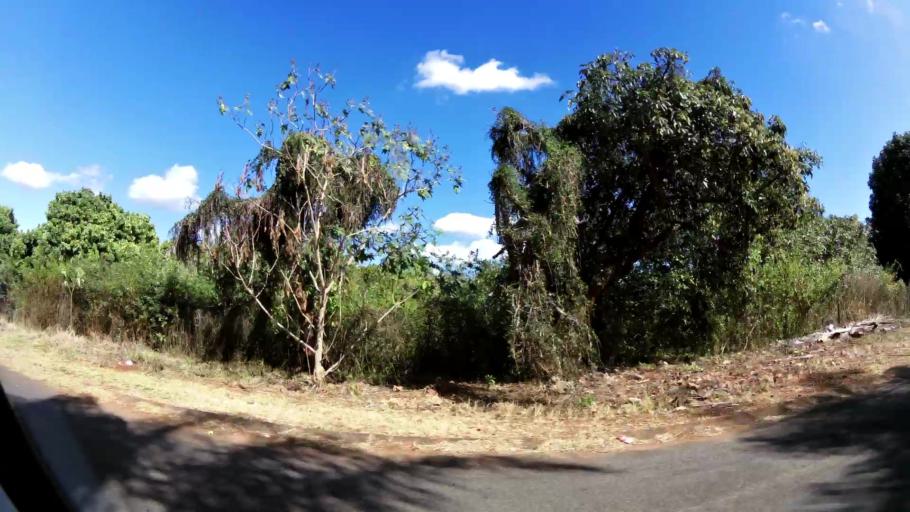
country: ZA
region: Limpopo
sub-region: Mopani District Municipality
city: Tzaneen
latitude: -23.8228
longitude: 30.1453
